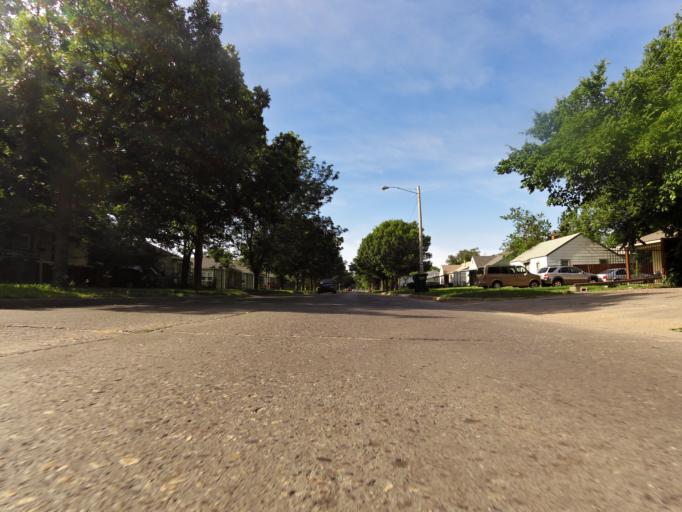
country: US
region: Kansas
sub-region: Sedgwick County
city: Wichita
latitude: 37.7075
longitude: -97.3082
